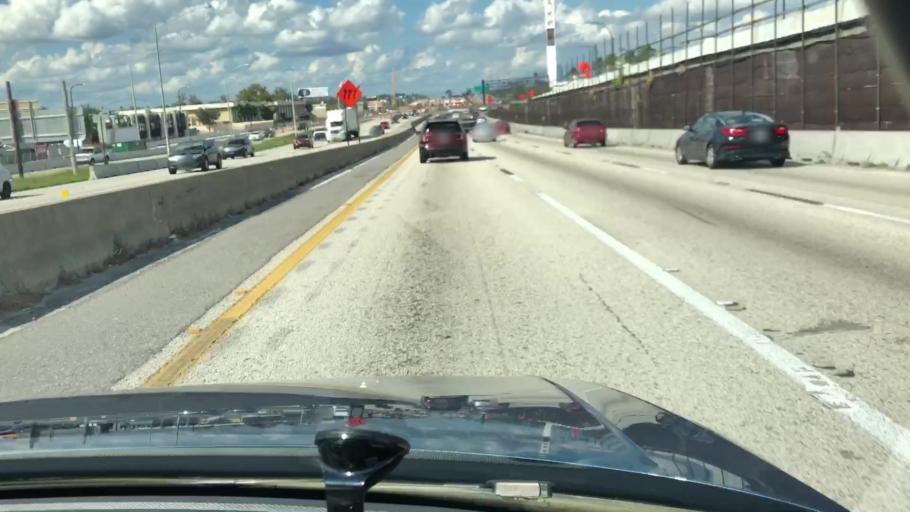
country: US
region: Florida
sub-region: Orange County
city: Eatonville
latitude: 28.6076
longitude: -81.3864
